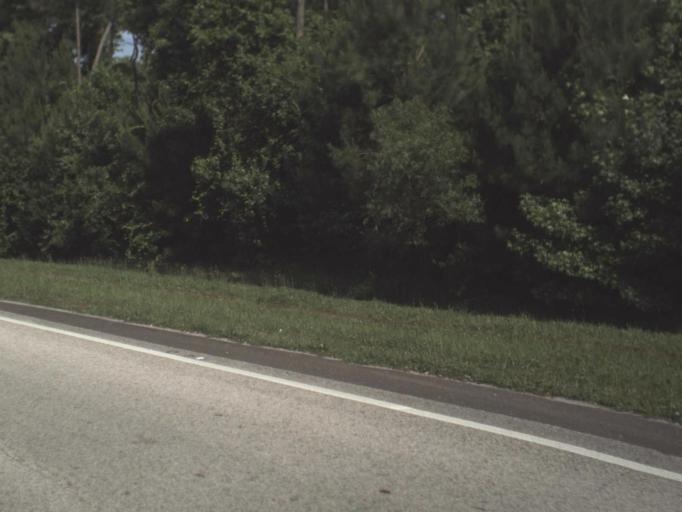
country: US
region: Florida
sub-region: Duval County
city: Jacksonville
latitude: 30.2501
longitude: -81.5578
